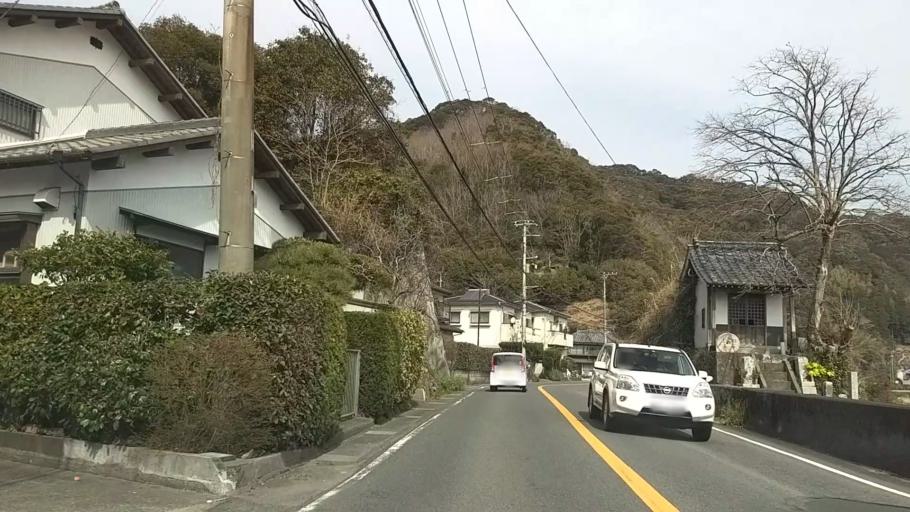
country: JP
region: Shizuoka
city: Shimoda
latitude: 34.7049
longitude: 138.9392
